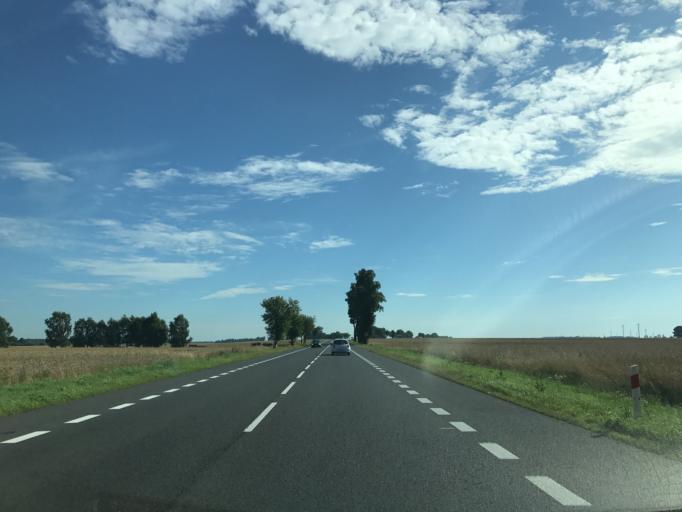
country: PL
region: West Pomeranian Voivodeship
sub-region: Powiat slawienski
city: Slawno
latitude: 54.3708
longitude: 16.7267
